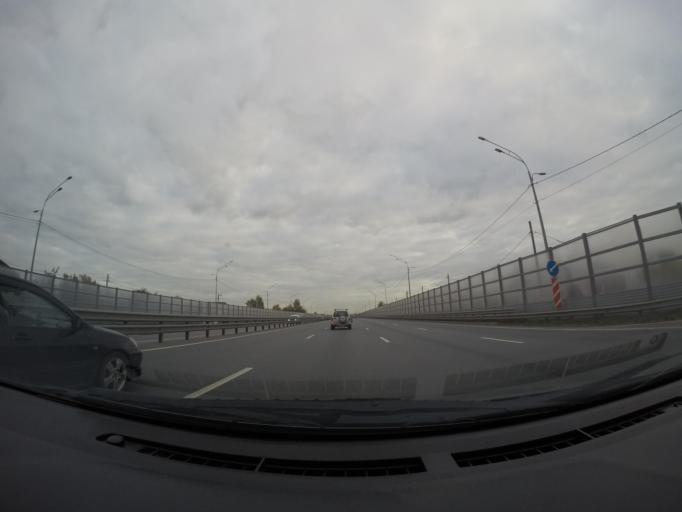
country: RU
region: Moskovskaya
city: Zheleznodorozhnyy
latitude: 55.8041
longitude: 38.0277
